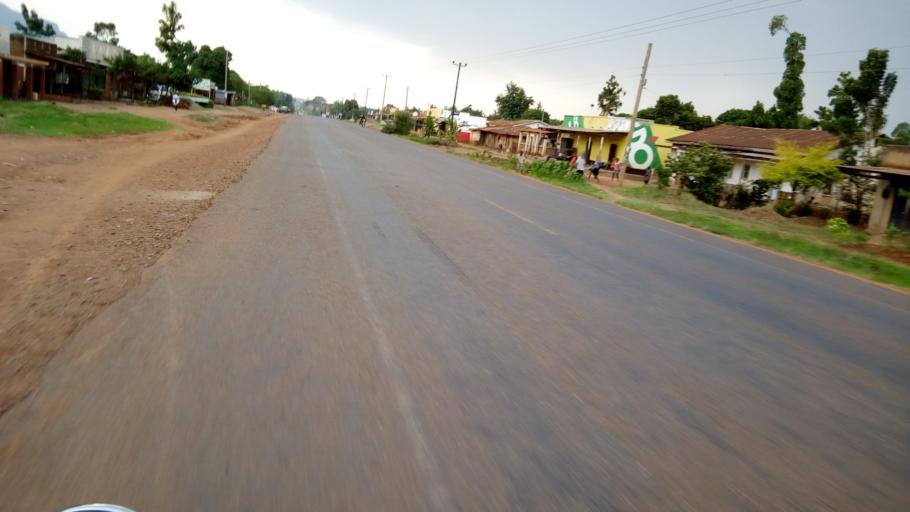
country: UG
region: Eastern Region
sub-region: Mbale District
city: Mbale
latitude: 1.1167
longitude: 34.1705
